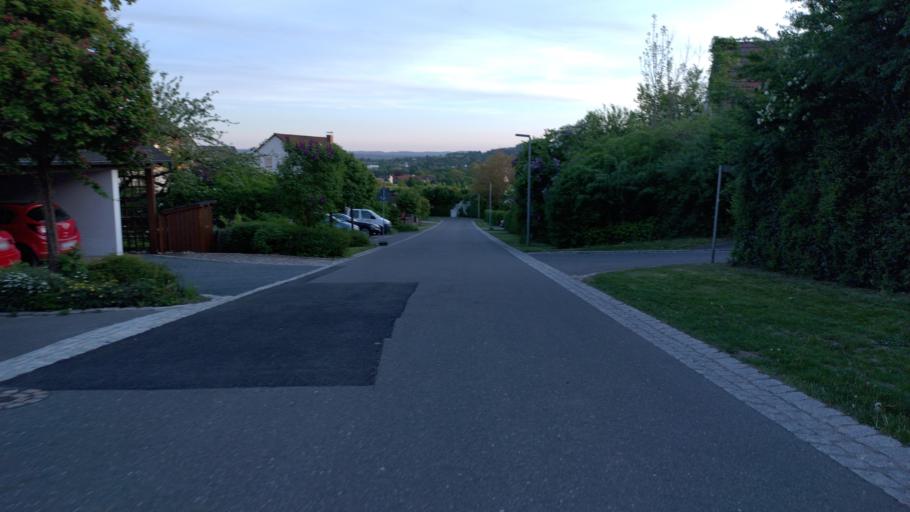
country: DE
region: Bavaria
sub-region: Upper Franconia
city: Bindlach
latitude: 49.9882
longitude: 11.6172
